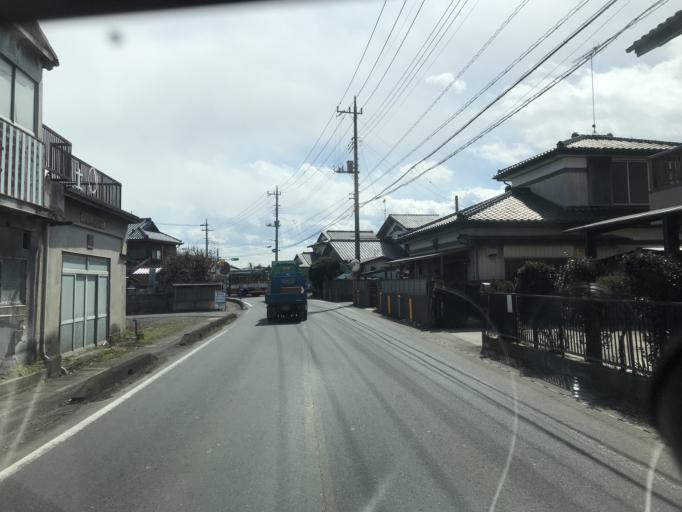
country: JP
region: Ibaraki
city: Yuki
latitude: 36.2584
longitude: 139.9138
